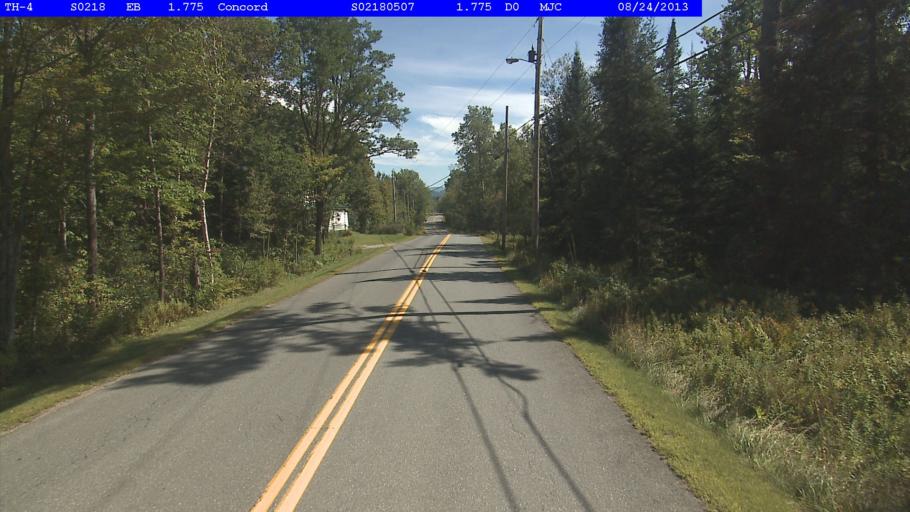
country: US
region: New Hampshire
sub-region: Grafton County
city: Littleton
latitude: 44.4416
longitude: -71.7619
